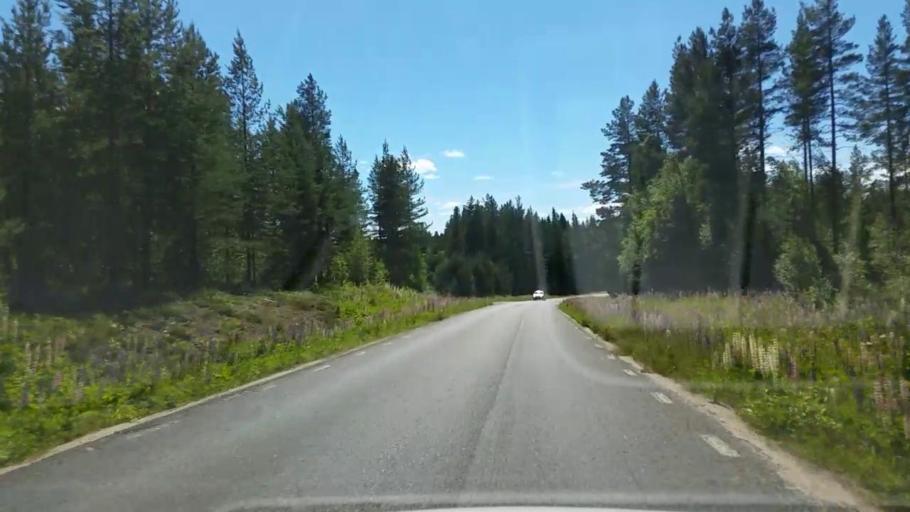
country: SE
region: Gaevleborg
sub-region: Ljusdals Kommun
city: Farila
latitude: 61.6699
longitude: 15.6144
